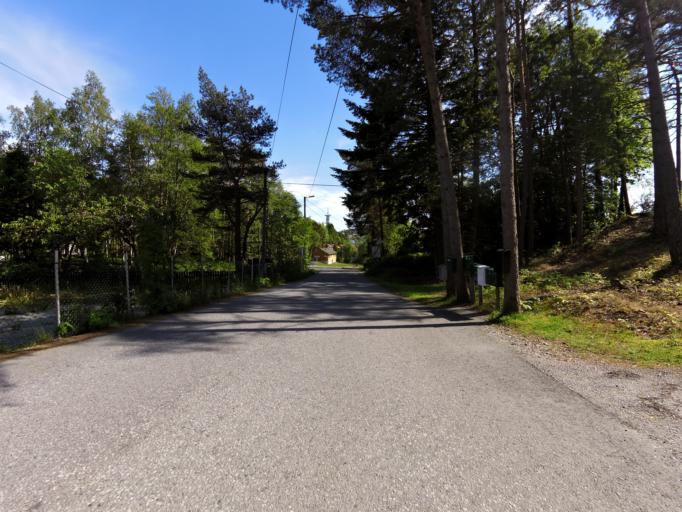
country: NO
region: Hordaland
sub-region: Stord
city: Leirvik
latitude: 59.7855
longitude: 5.4981
